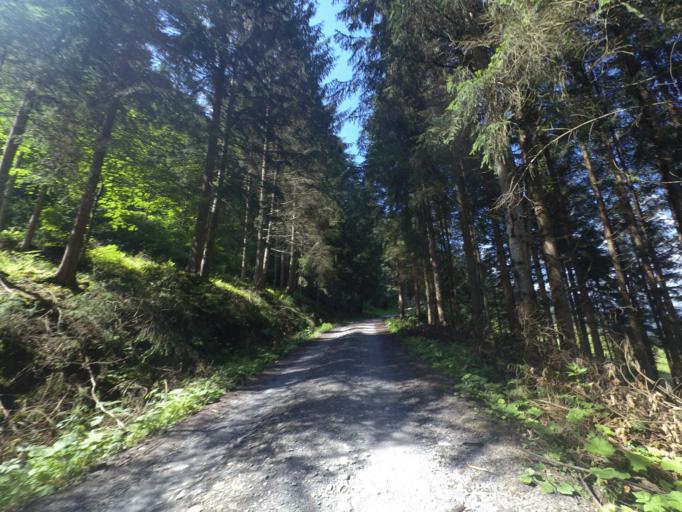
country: AT
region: Salzburg
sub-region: Politischer Bezirk Sankt Johann im Pongau
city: Schwarzach im Pongau
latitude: 47.3075
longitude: 13.1404
